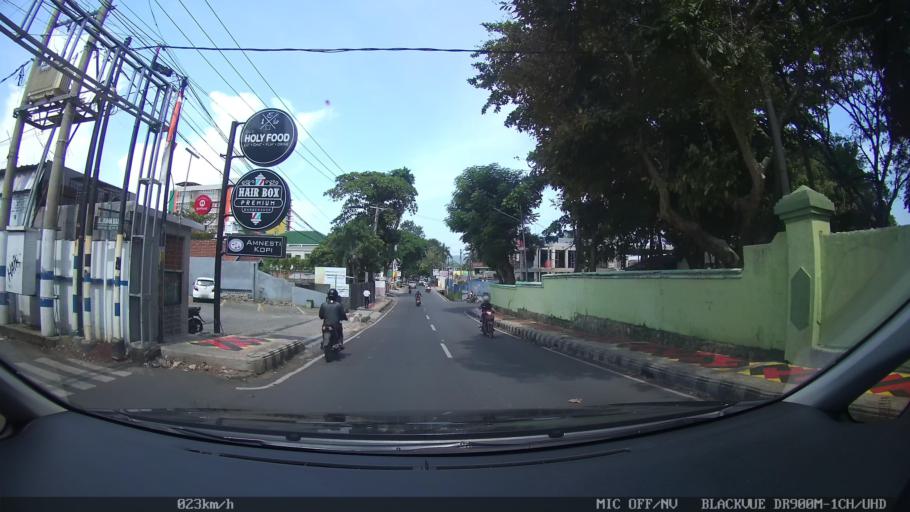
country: ID
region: Lampung
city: Bandarlampung
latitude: -5.4178
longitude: 105.2598
